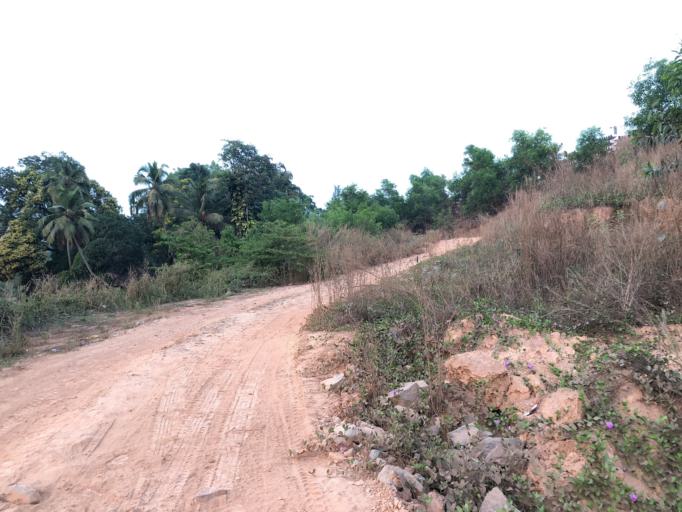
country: IN
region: Karnataka
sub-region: Dakshina Kannada
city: Mangalore
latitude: 12.8719
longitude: 74.8912
